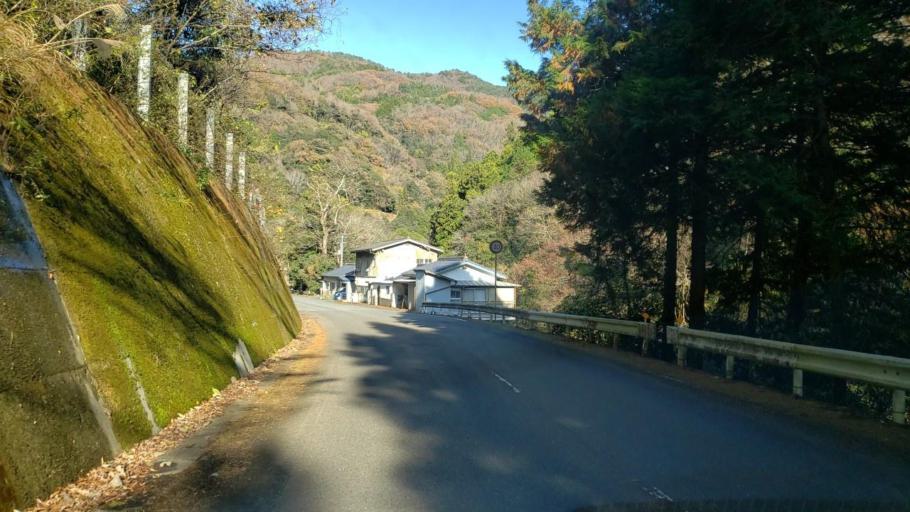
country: JP
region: Tokushima
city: Wakimachi
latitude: 34.0193
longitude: 134.0372
